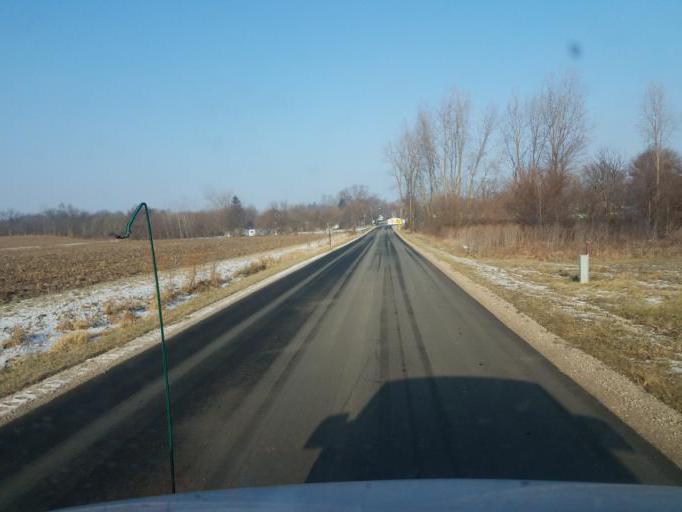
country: US
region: Ohio
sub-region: Crawford County
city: Galion
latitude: 40.6656
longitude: -82.8404
